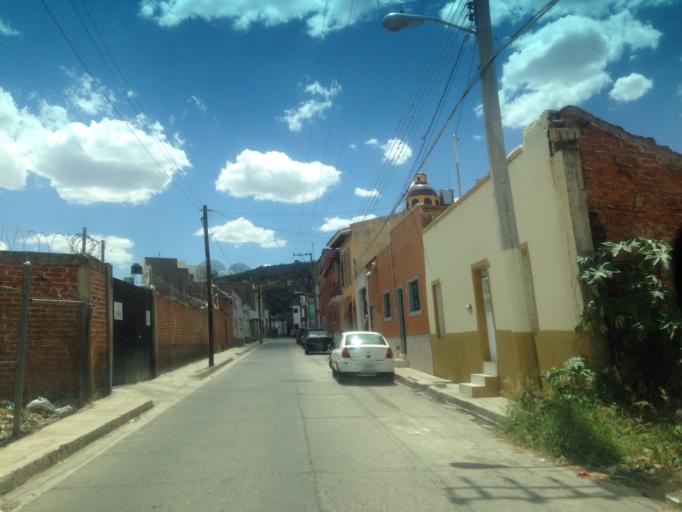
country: MX
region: Jalisco
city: Atotonilco el Alto
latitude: 20.5531
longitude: -102.5039
